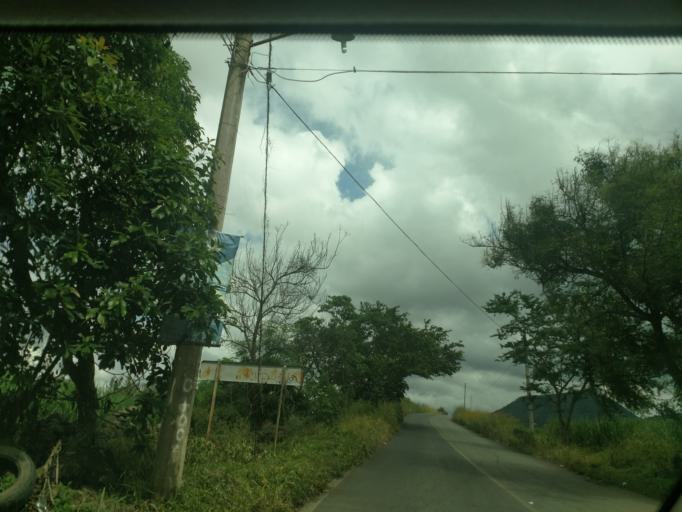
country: MX
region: Nayarit
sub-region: Tepic
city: La Corregidora
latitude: 21.4512
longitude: -104.8107
